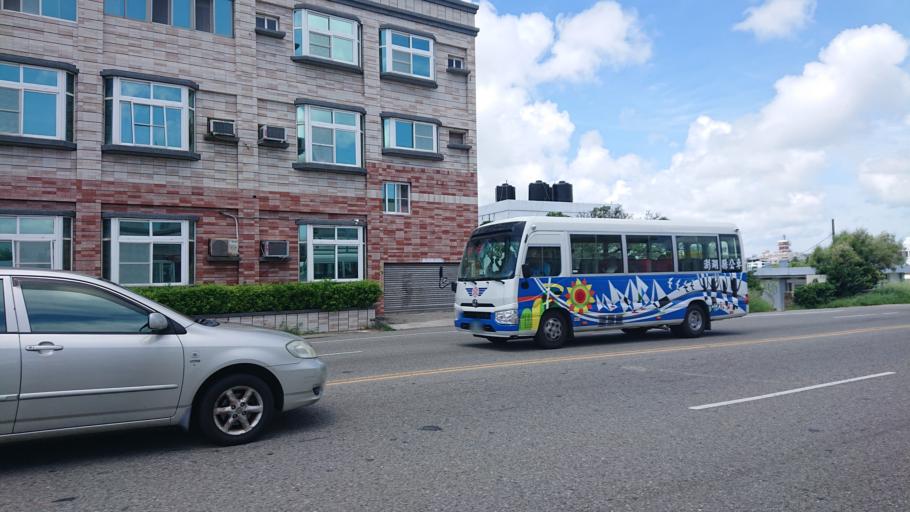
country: TW
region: Taiwan
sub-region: Penghu
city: Ma-kung
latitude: 23.5689
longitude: 119.5925
